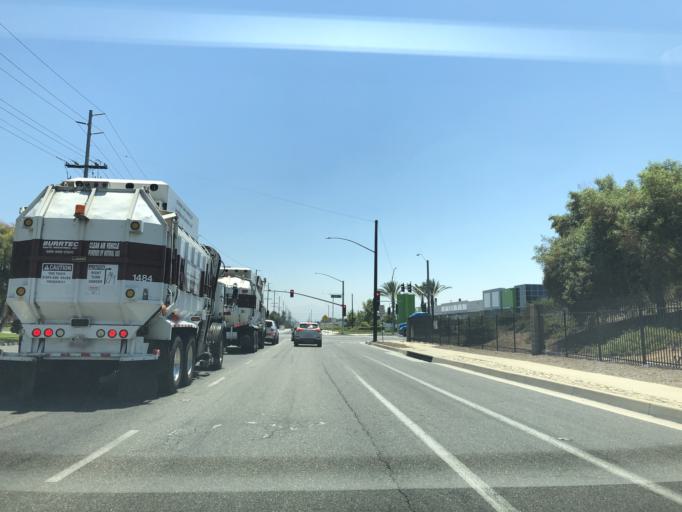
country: US
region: California
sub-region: San Bernardino County
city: Rancho Cucamonga
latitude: 34.0998
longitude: -117.5239
